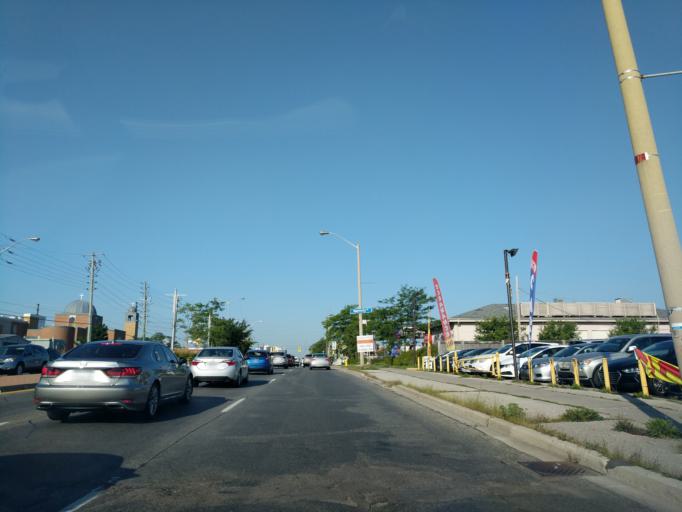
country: CA
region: Ontario
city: Scarborough
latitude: 43.7500
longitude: -79.2733
